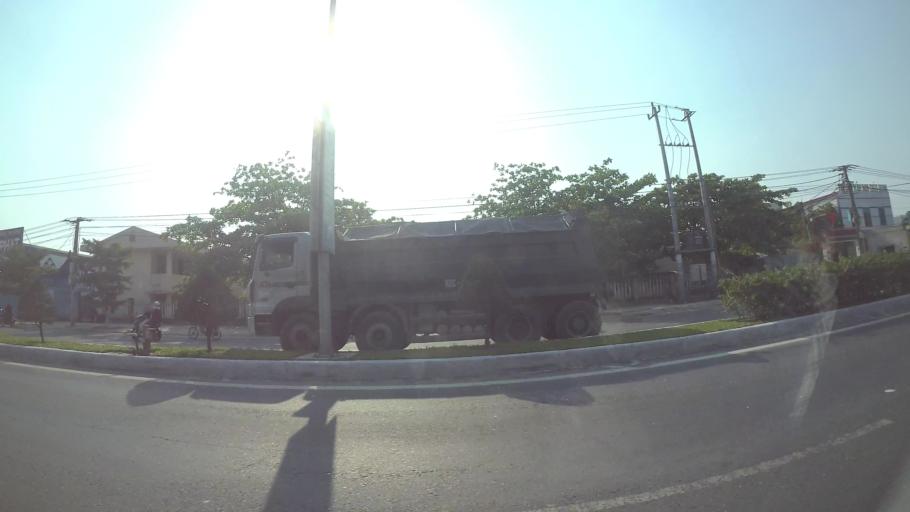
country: VN
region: Quang Nam
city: Quang Nam
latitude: 15.9434
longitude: 108.2547
